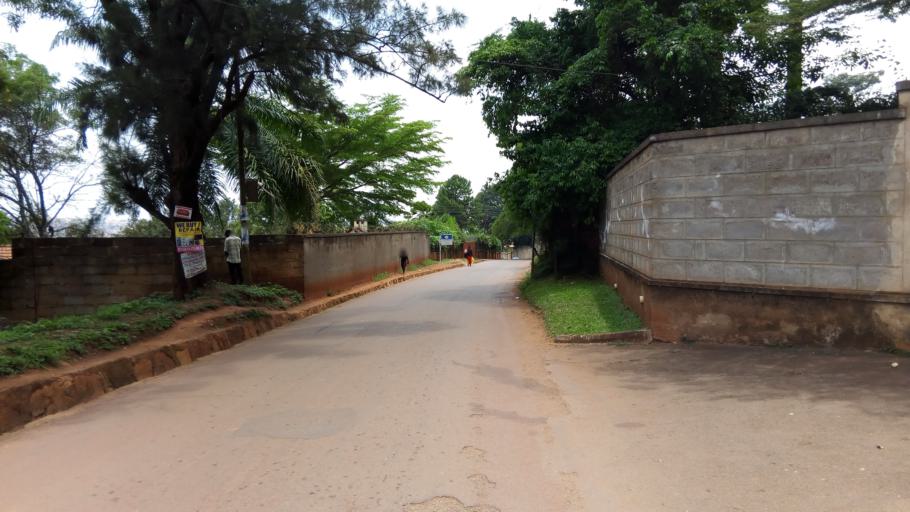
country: UG
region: Central Region
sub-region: Wakiso District
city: Kireka
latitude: 0.3217
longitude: 32.6265
